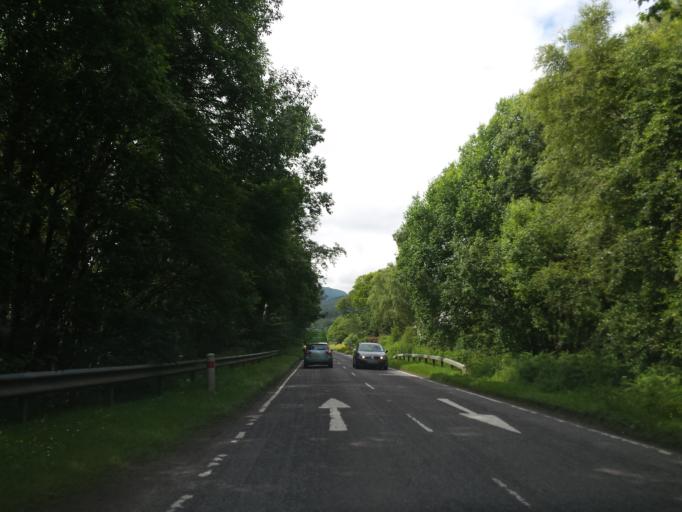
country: GB
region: Scotland
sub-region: Highland
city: Fort William
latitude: 56.8481
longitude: -5.1613
